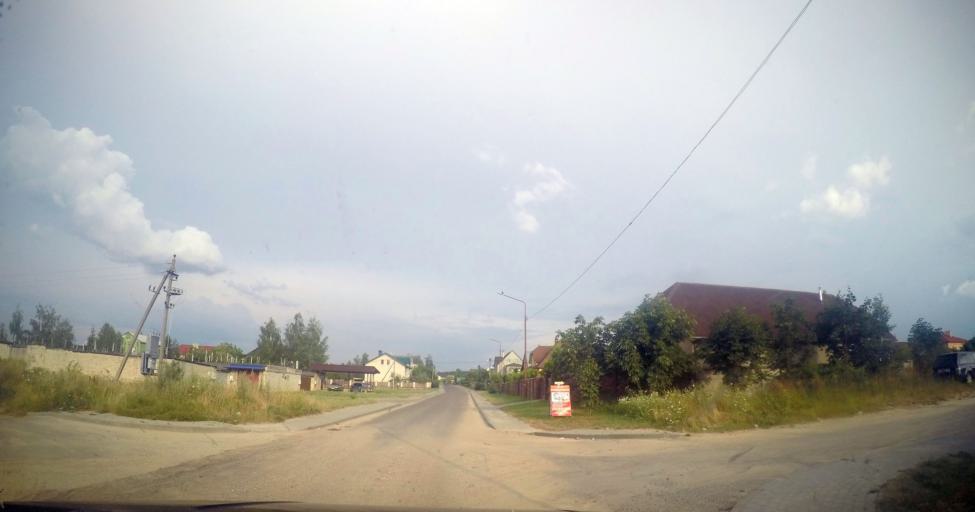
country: BY
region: Grodnenskaya
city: Hrodna
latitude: 53.6241
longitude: 23.8388
